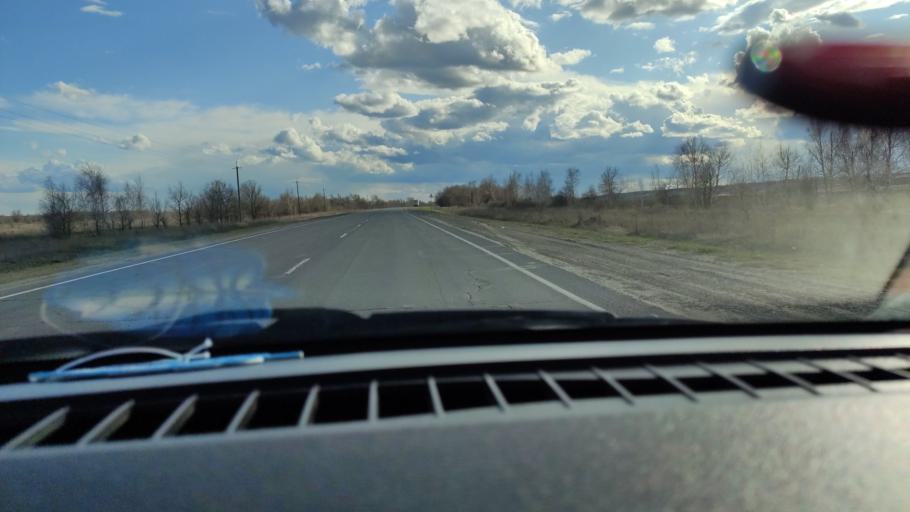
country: RU
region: Saratov
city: Sinodskoye
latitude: 52.0335
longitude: 46.7257
